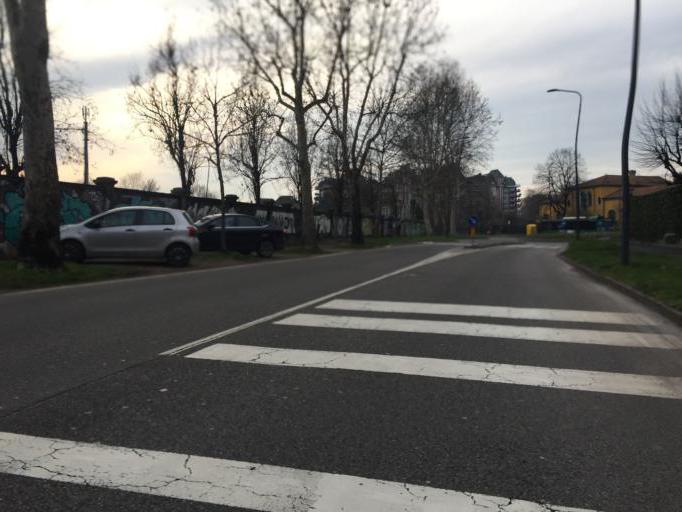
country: IT
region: Lombardy
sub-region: Citta metropolitana di Milano
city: Baranzate
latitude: 45.4857
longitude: 9.1261
